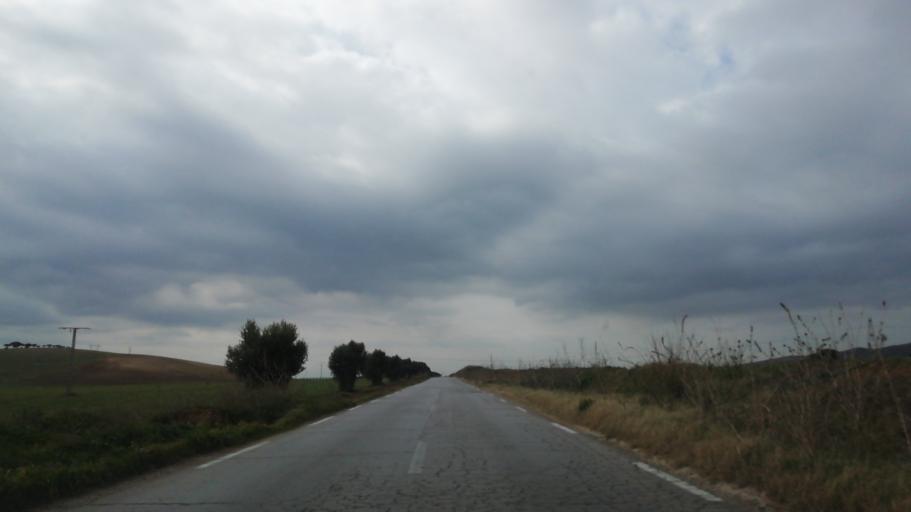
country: DZ
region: Oran
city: Sidi ech Chahmi
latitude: 35.6282
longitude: -0.4018
